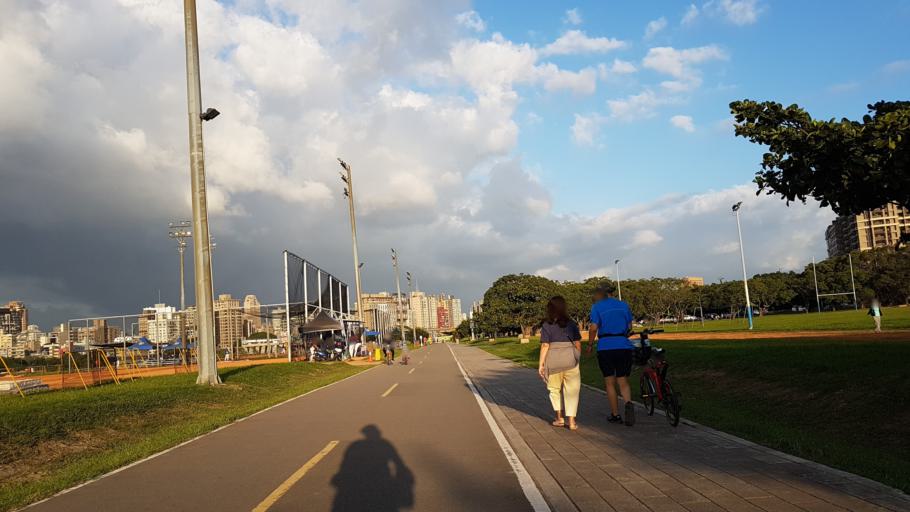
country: TW
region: Taipei
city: Taipei
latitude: 25.0189
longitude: 121.5107
